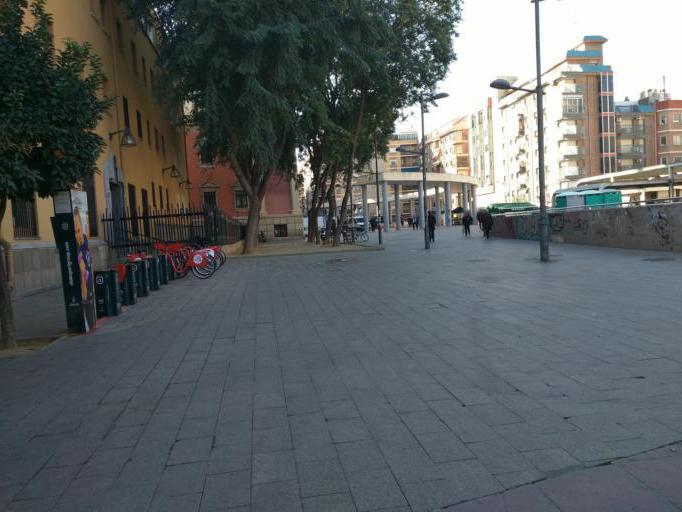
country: ES
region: Murcia
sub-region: Murcia
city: Murcia
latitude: 37.9882
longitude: -1.1250
